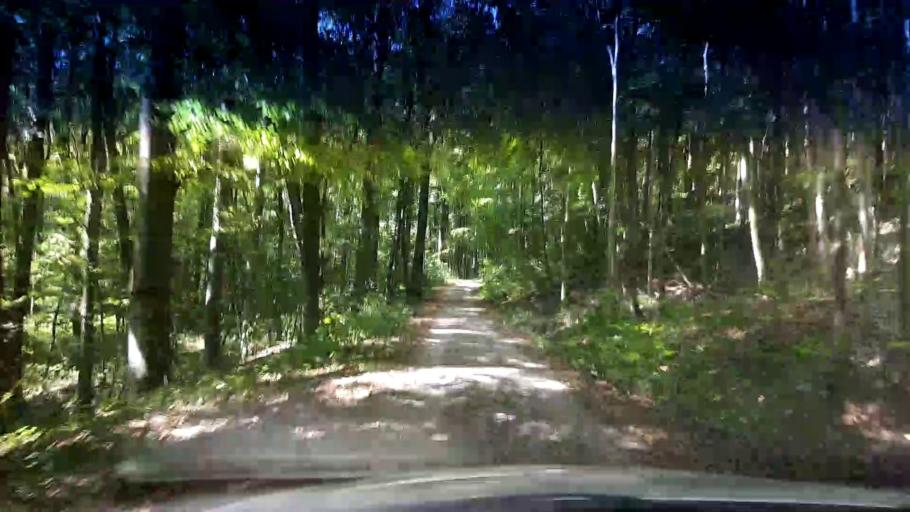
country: DE
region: Bavaria
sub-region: Upper Franconia
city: Schesslitz
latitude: 49.9488
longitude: 11.0658
